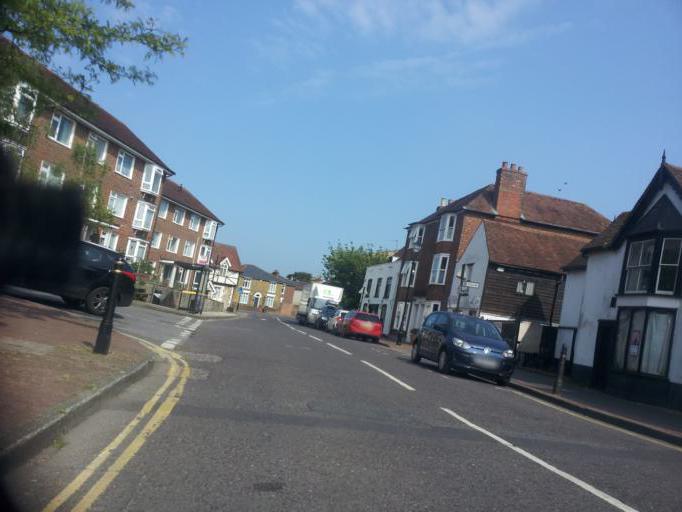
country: GB
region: England
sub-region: Kent
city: Aylesford
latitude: 51.3036
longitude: 0.4806
